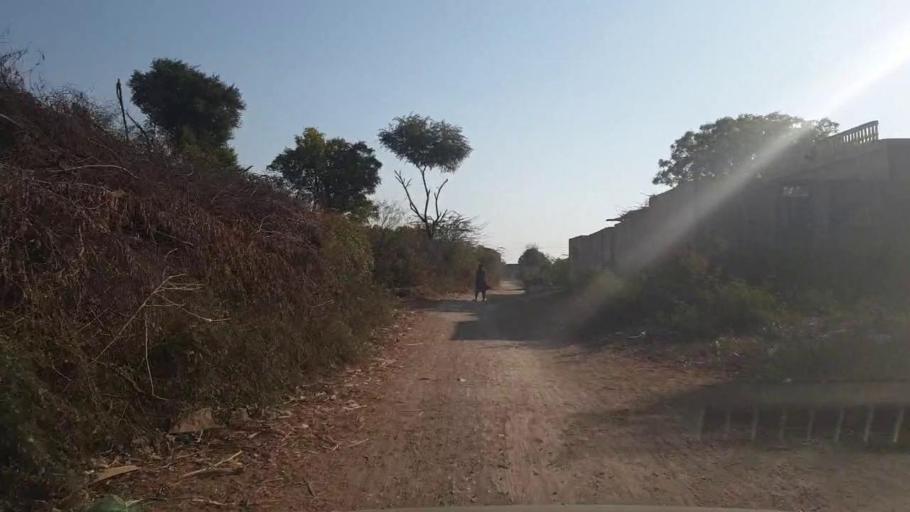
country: PK
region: Sindh
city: Chambar
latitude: 25.2935
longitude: 68.7687
